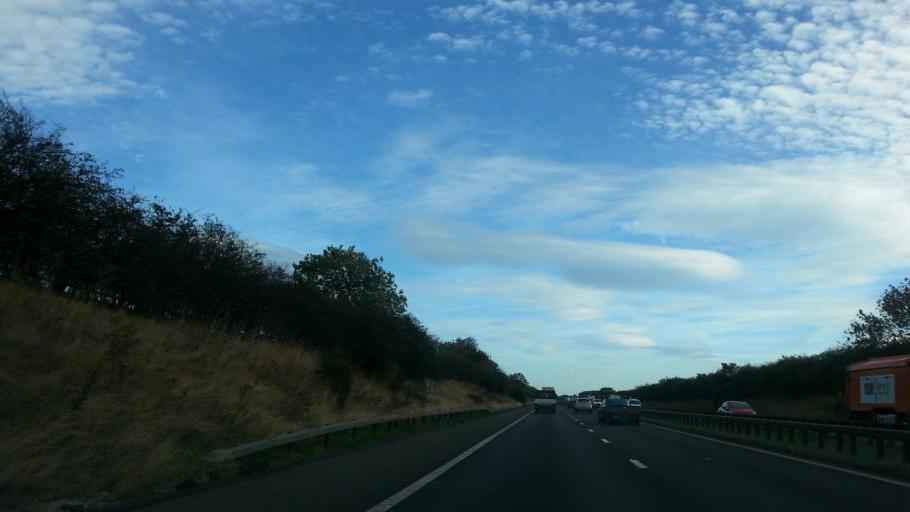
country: GB
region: England
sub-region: Doncaster
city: Marr
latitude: 53.5357
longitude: -1.1984
